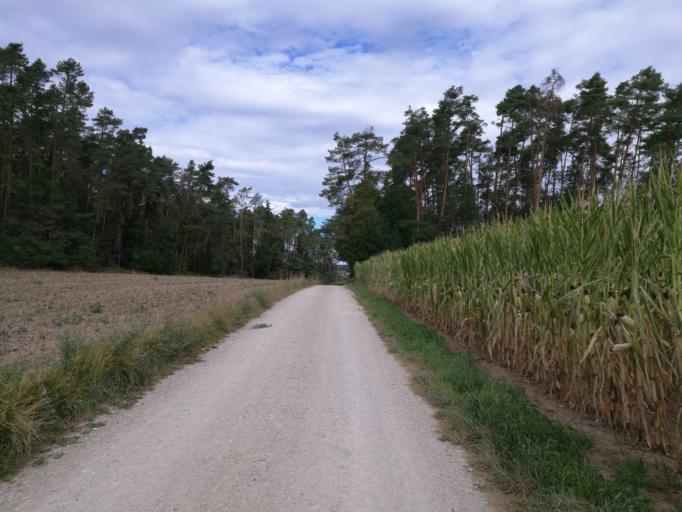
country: DE
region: Bavaria
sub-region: Regierungsbezirk Mittelfranken
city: Seukendorf
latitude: 49.4752
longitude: 10.8955
